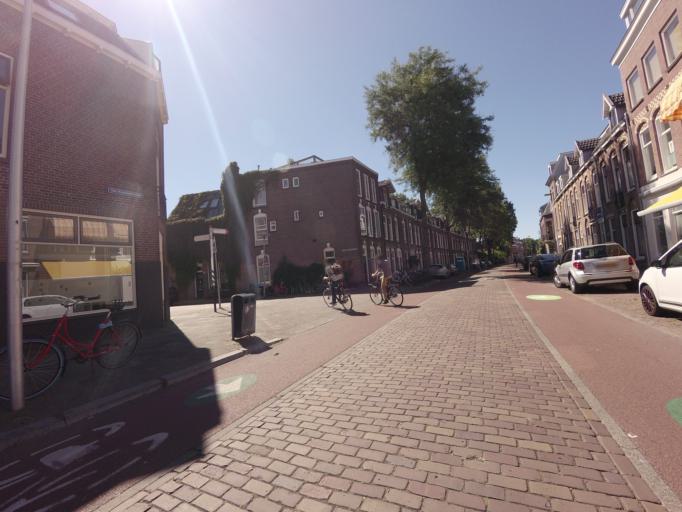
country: NL
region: Utrecht
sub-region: Gemeente Utrecht
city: Utrecht
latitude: 52.0997
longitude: 5.1223
